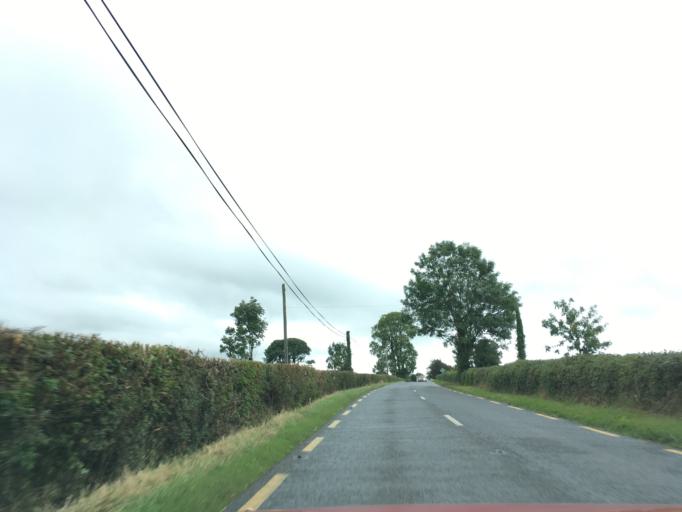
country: IE
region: Munster
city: Fethard
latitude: 52.4266
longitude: -7.7752
